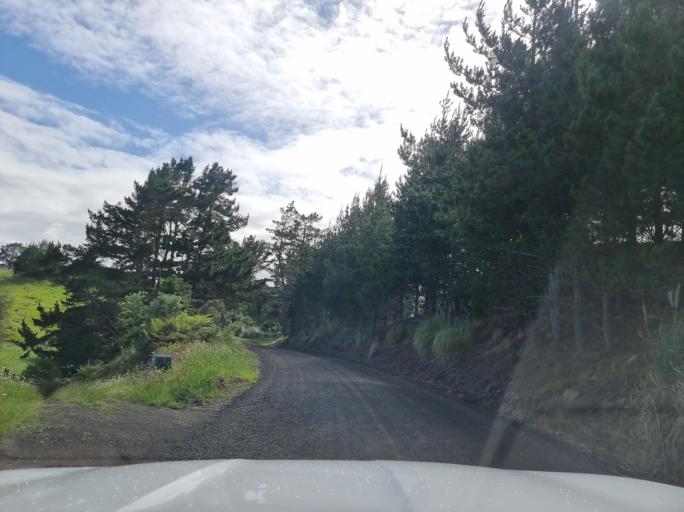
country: NZ
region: Northland
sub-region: Whangarei
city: Maungatapere
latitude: -35.8101
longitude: 174.0405
